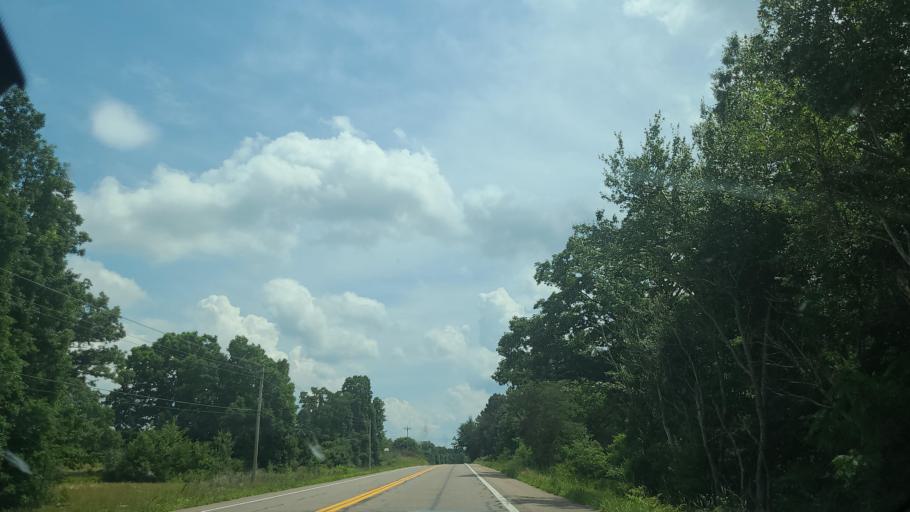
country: US
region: Tennessee
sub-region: Cumberland County
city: Lake Tansi
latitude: 35.8750
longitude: -85.0036
